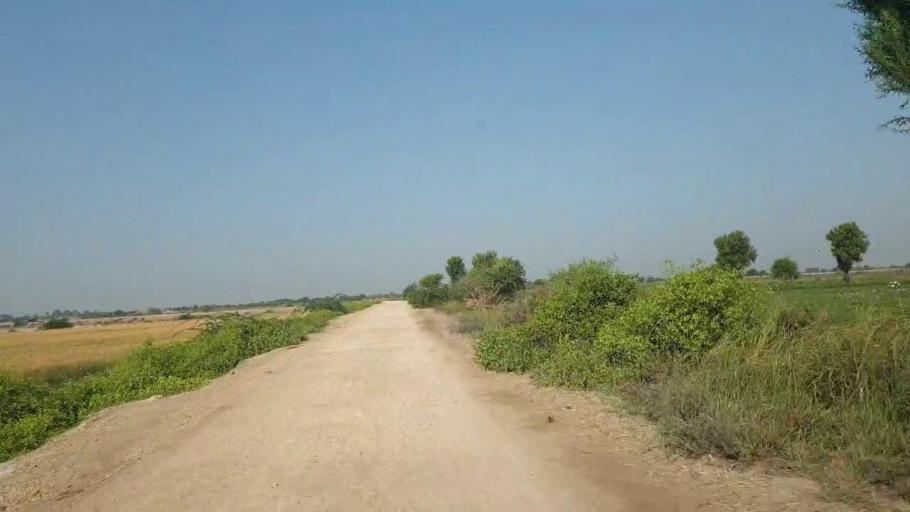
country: PK
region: Sindh
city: Badin
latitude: 24.5208
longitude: 68.7735
